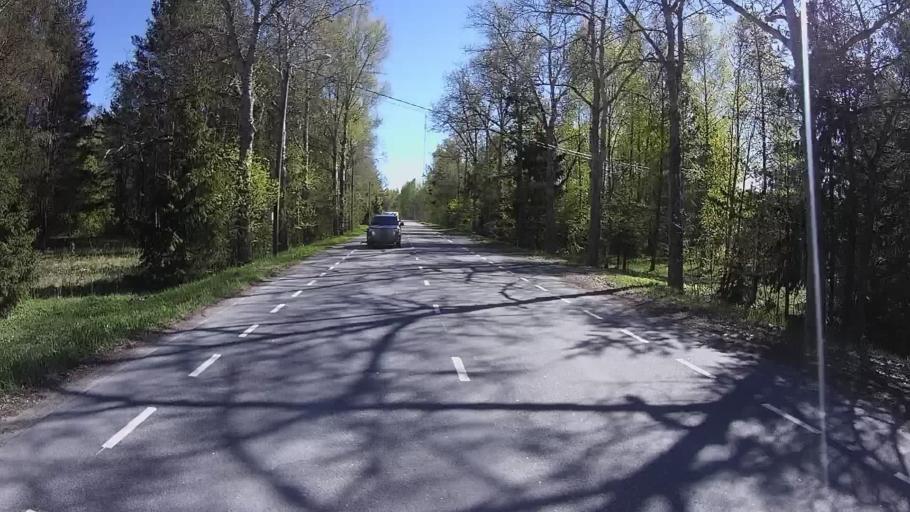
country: EE
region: Harju
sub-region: Loksa linn
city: Loksa
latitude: 59.5724
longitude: 25.7247
